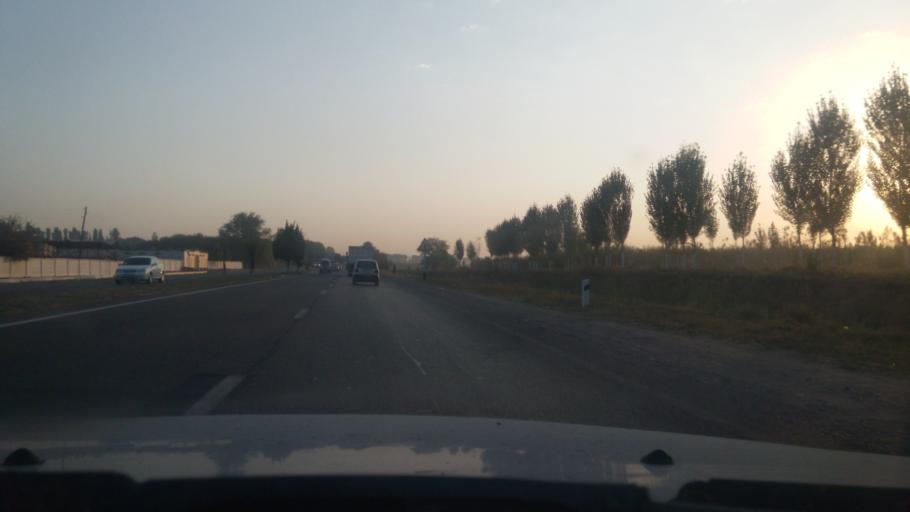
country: UZ
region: Toshkent
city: Yangiyul
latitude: 41.1667
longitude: 69.0597
